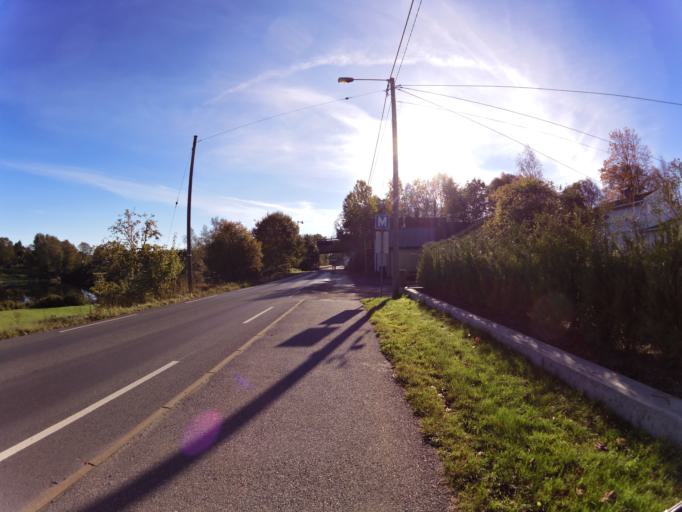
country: NO
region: Ostfold
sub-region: Sarpsborg
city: Sarpsborg
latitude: 59.2701
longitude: 11.0222
